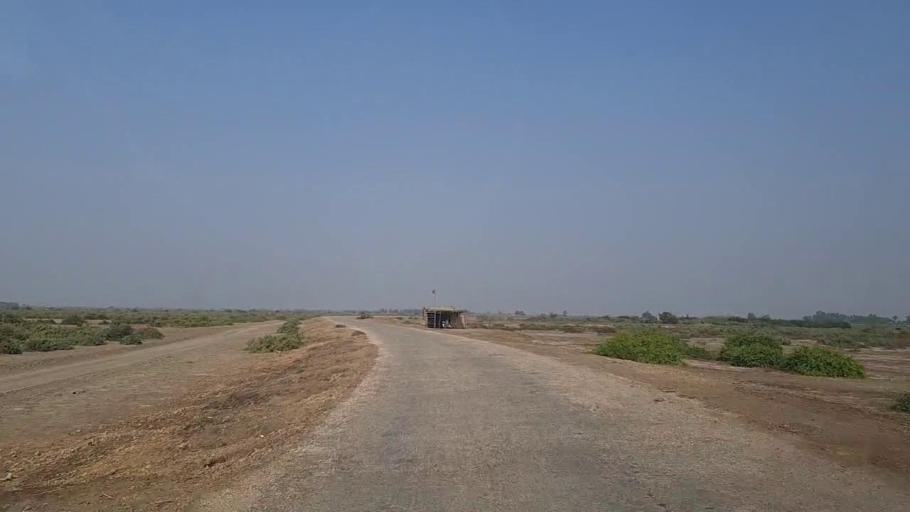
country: PK
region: Sindh
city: Keti Bandar
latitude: 24.2427
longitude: 67.6930
